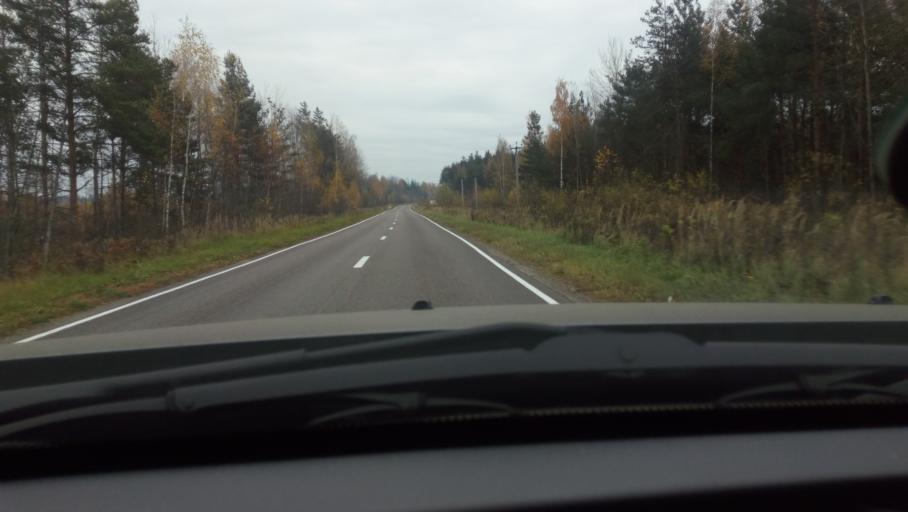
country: RU
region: Moskovskaya
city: Avsyunino
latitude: 55.5878
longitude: 39.2631
